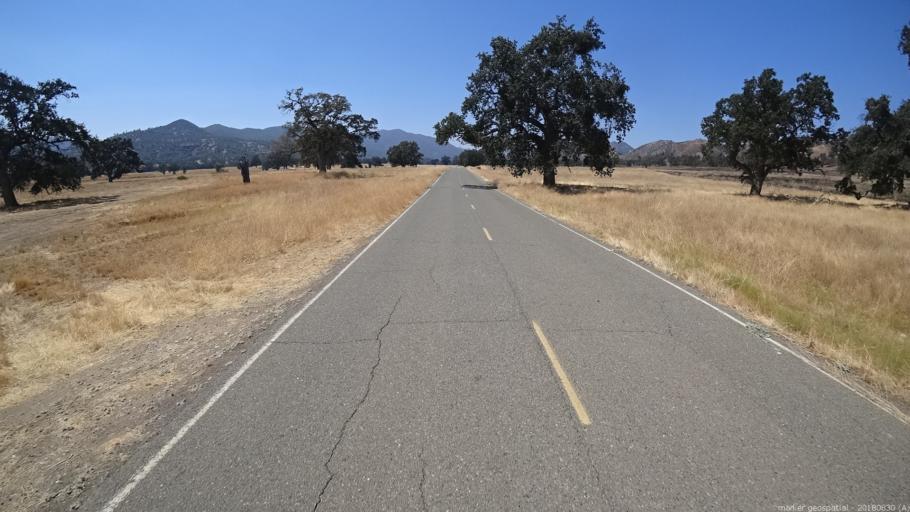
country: US
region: California
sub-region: Monterey County
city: King City
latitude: 35.9653
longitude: -121.3015
